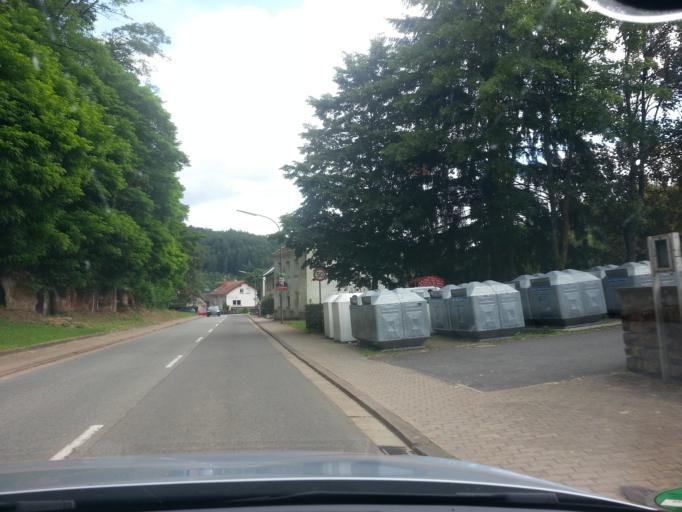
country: DE
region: Saarland
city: Beckingen
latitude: 49.4306
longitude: 6.7276
